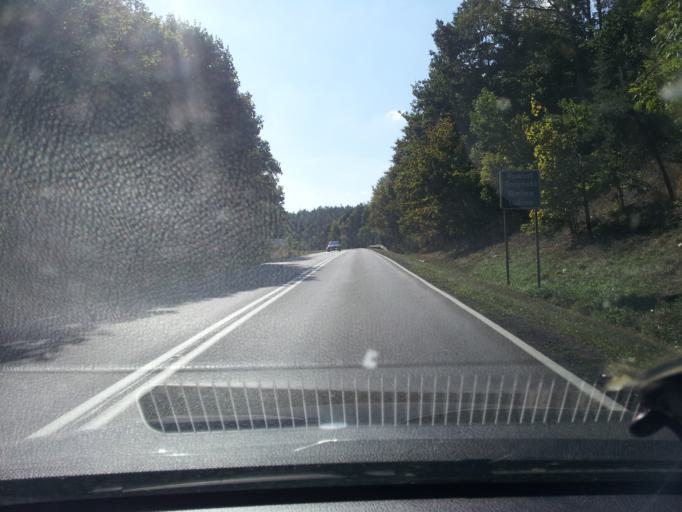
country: PL
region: Kujawsko-Pomorskie
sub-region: Powiat torunski
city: Lubicz Gorny
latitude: 53.1137
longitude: 18.8108
